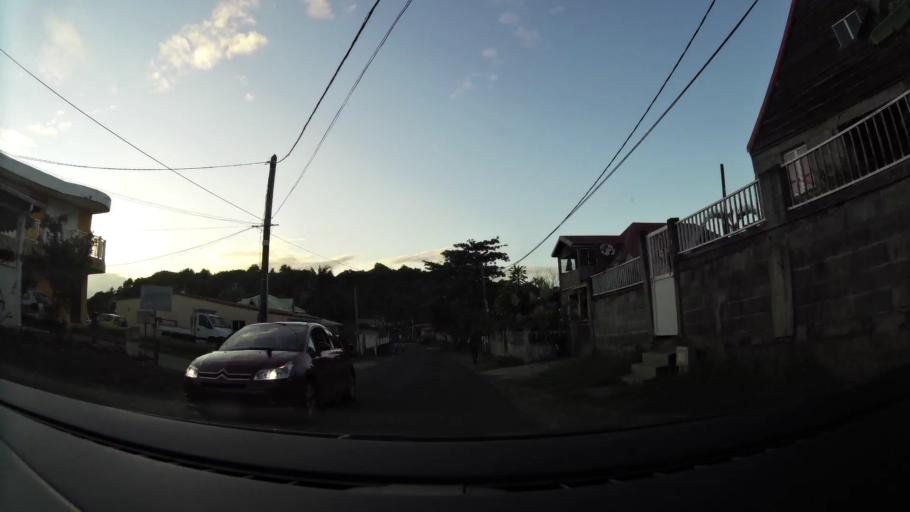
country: GP
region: Guadeloupe
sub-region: Guadeloupe
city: Les Abymes
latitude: 16.2700
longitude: -61.4974
